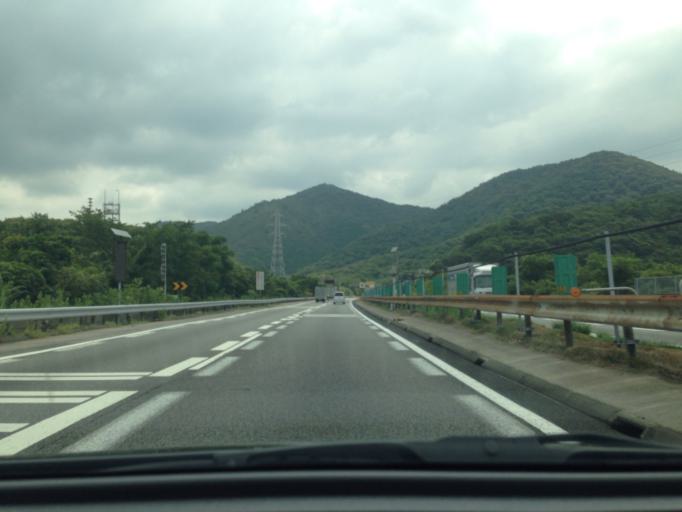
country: JP
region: Aichi
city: Shinshiro
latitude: 34.8455
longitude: 137.5158
